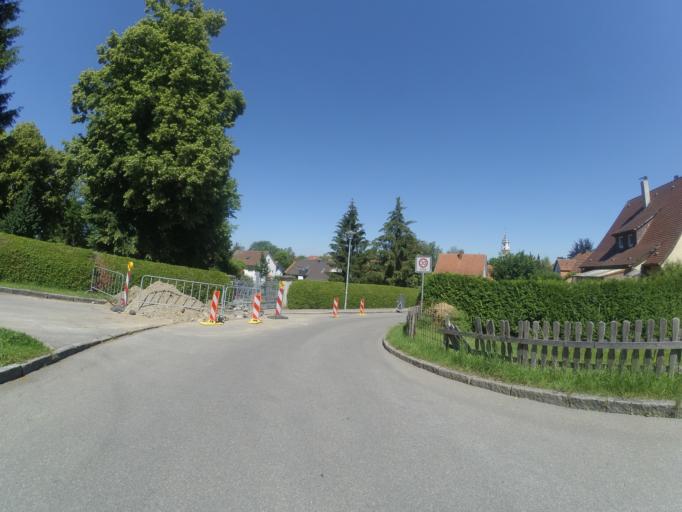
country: DE
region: Baden-Wuerttemberg
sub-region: Tuebingen Region
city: Bad Wurzach
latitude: 47.9065
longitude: 9.9007
